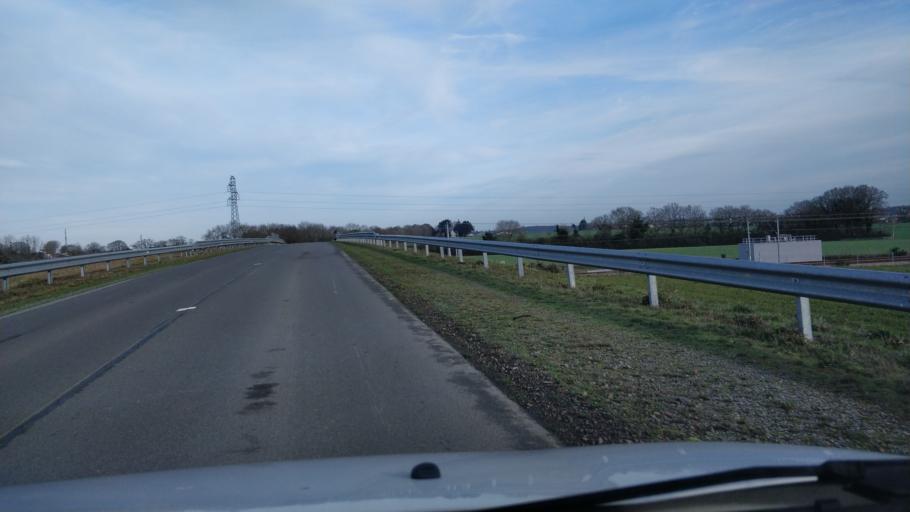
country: FR
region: Brittany
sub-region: Departement d'Ille-et-Vilaine
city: Argentre-du-Plessis
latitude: 48.0427
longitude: -1.1680
